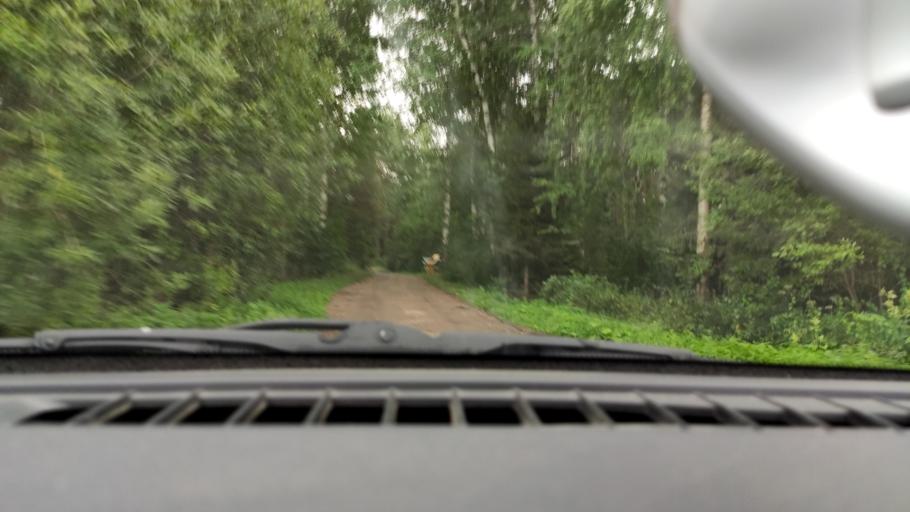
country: RU
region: Perm
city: Overyata
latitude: 58.0527
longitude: 55.9768
